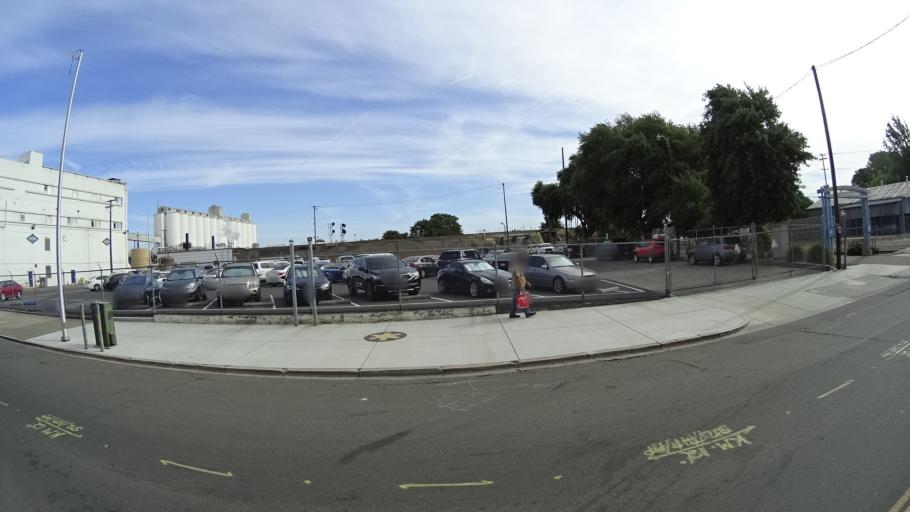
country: US
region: California
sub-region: Sacramento County
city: Sacramento
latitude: 38.5845
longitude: -121.4775
